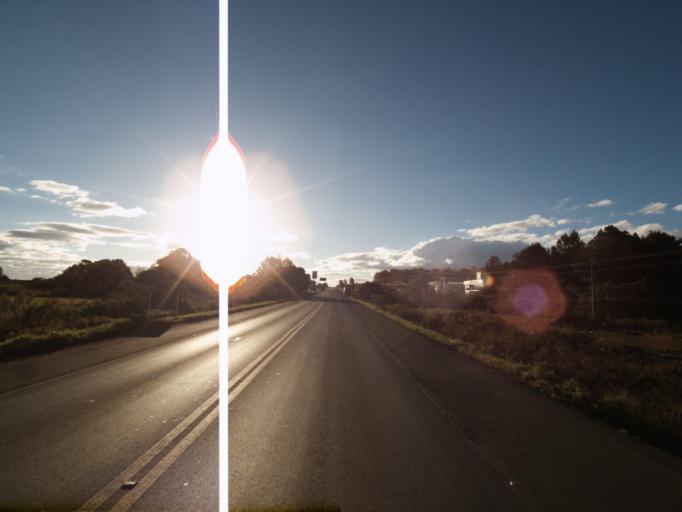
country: BR
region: Santa Catarina
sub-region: Campos Novos
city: Campos Novos
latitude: -27.3841
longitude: -51.2369
